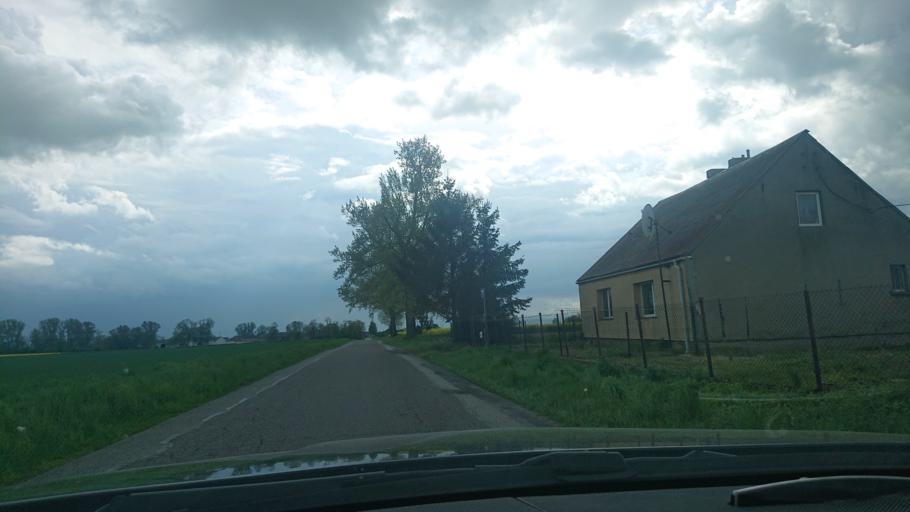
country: PL
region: Greater Poland Voivodeship
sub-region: Powiat gnieznienski
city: Niechanowo
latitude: 52.4749
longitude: 17.6358
